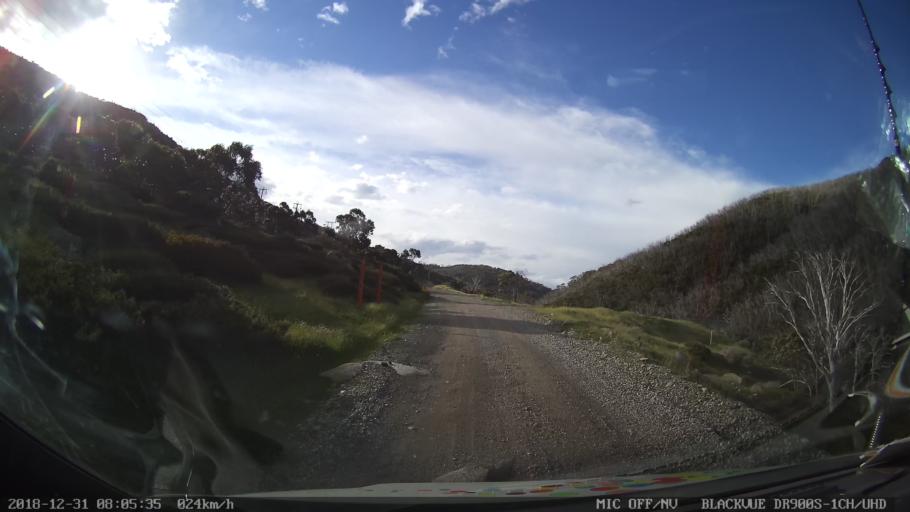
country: AU
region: New South Wales
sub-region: Snowy River
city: Jindabyne
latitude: -36.3716
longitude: 148.4067
